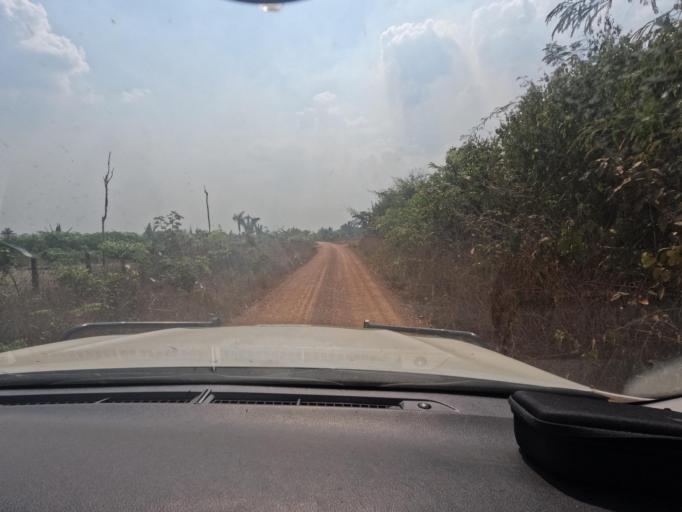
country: BR
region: Rondonia
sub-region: Porto Velho
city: Porto Velho
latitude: -8.7729
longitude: -63.1729
